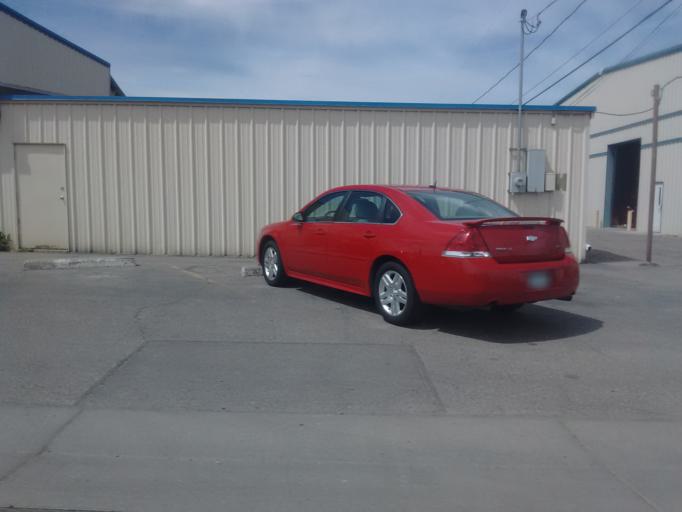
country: US
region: Colorado
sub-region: Mesa County
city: Grand Junction
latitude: 39.0606
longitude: -108.5577
